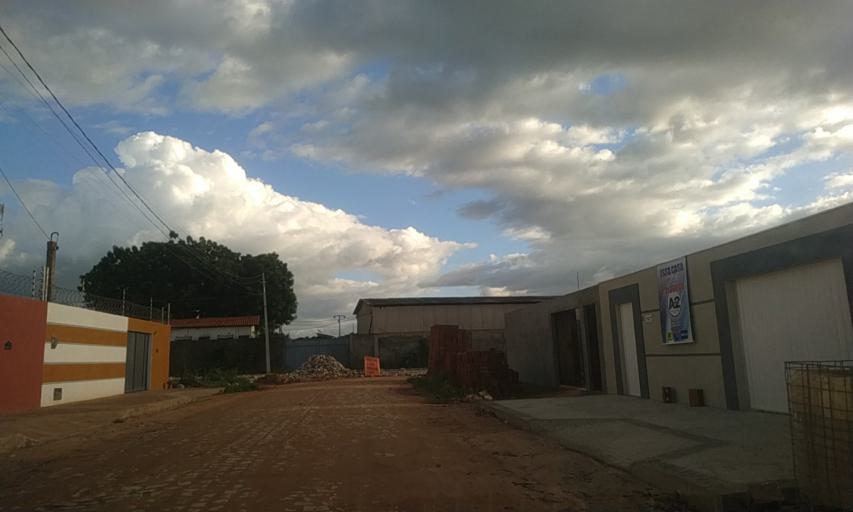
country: BR
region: Rio Grande do Norte
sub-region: Mossoro
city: Mossoro
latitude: -5.2229
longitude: -37.3436
